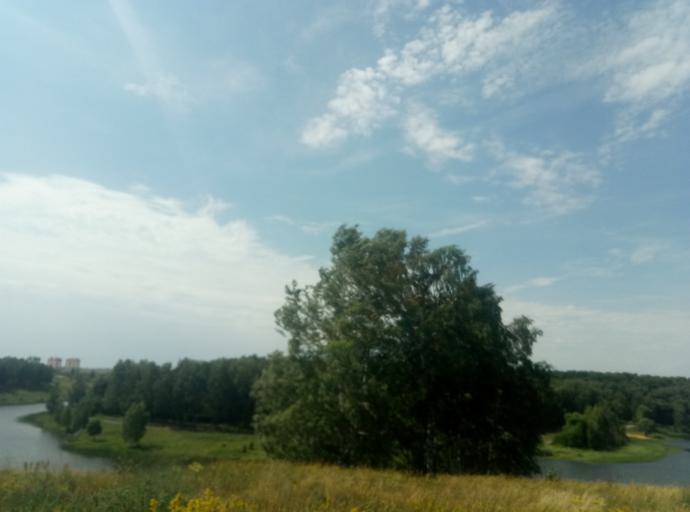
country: RU
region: Tula
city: Kireyevsk
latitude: 53.9320
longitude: 37.9488
